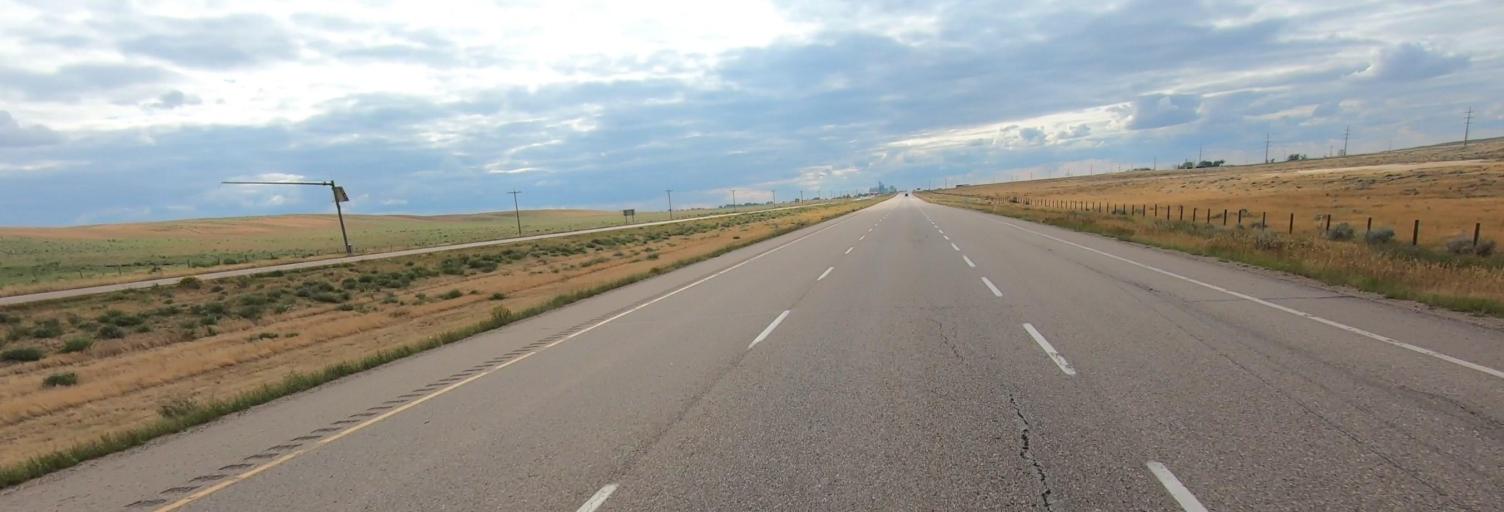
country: CA
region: Alberta
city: Medicine Hat
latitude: 49.9761
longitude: -110.5364
